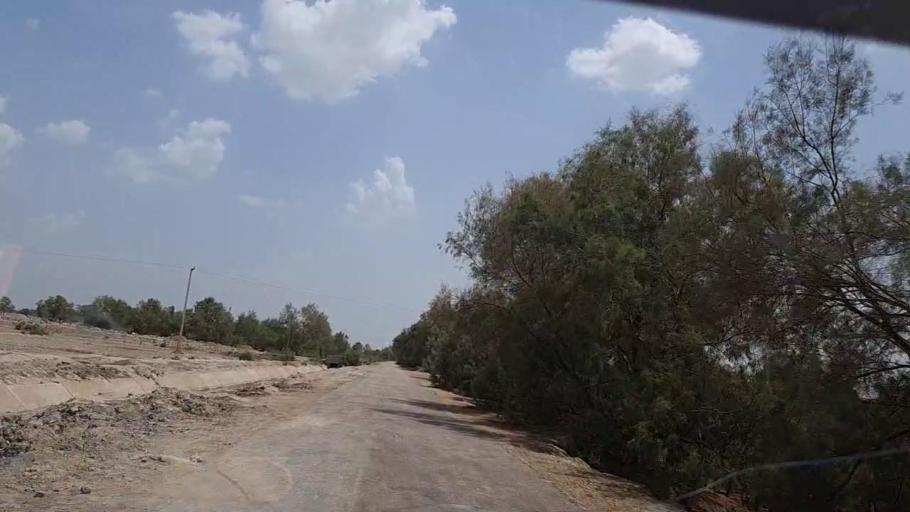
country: PK
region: Sindh
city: Bhan
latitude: 26.5106
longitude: 67.6407
